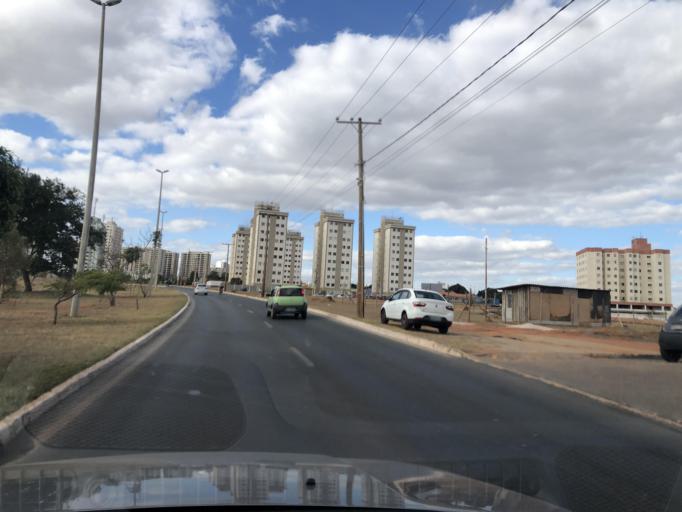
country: BR
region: Federal District
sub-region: Brasilia
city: Brasilia
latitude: -15.8887
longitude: -48.0954
